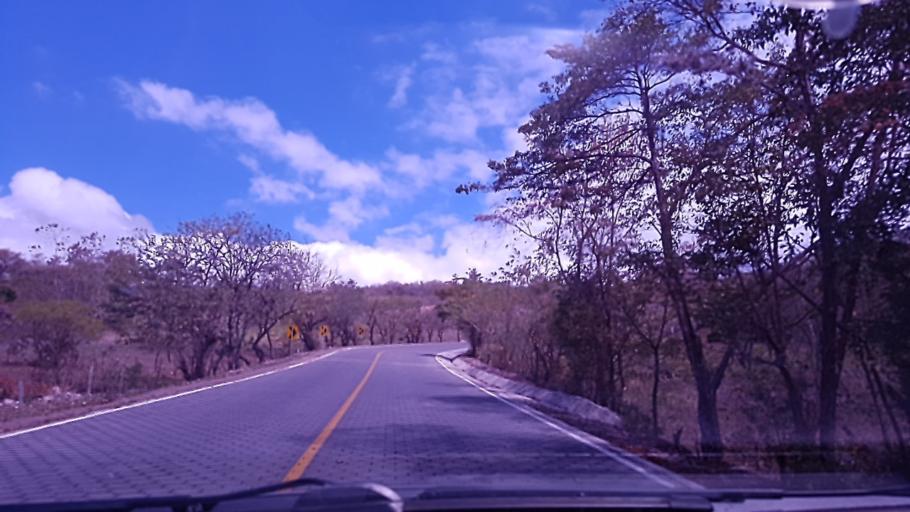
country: NI
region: Esteli
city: Condega
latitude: 13.4068
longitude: -86.2934
